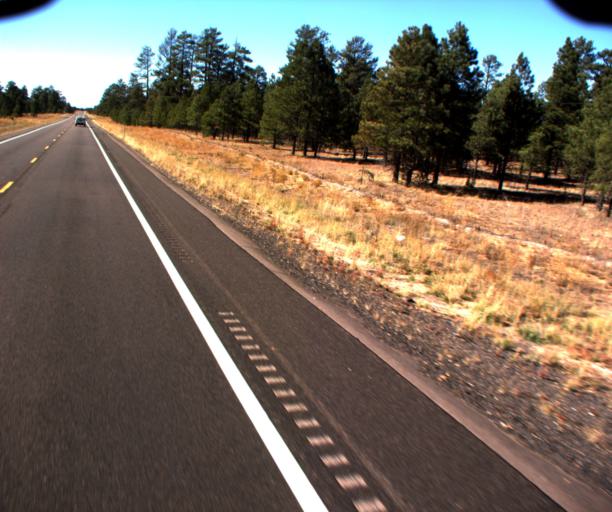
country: US
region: Arizona
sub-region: Apache County
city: Saint Michaels
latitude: 35.6986
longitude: -109.2838
